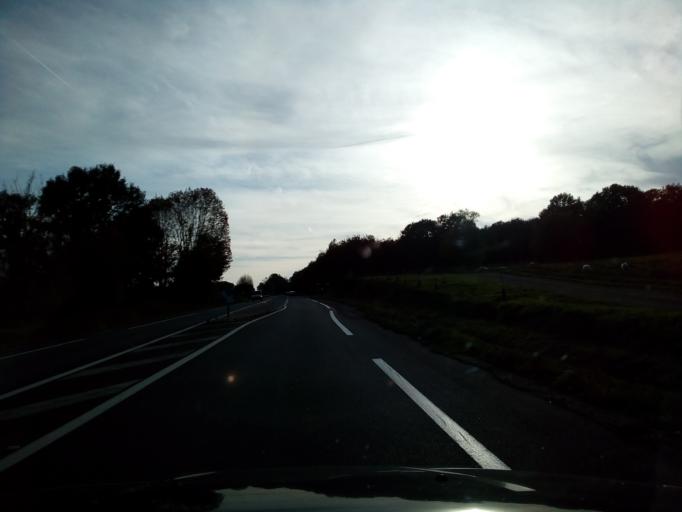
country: FR
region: Poitou-Charentes
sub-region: Departement de la Charente
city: Confolens
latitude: 45.9972
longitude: 0.6312
